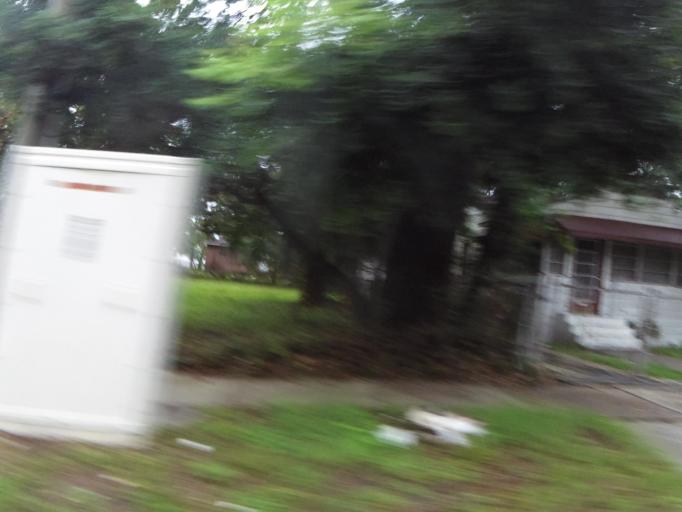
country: US
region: Florida
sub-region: Duval County
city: Jacksonville
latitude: 30.3494
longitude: -81.6331
